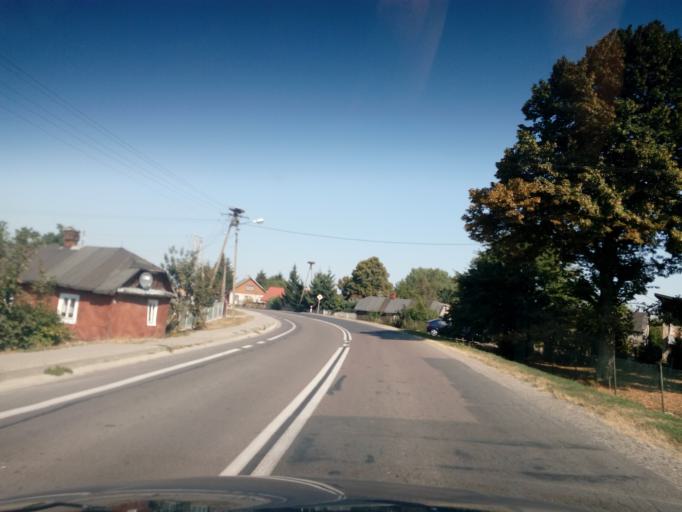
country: PL
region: Lublin Voivodeship
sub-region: Powiat hrubieszowski
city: Horodlo
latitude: 50.8337
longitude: 23.9771
